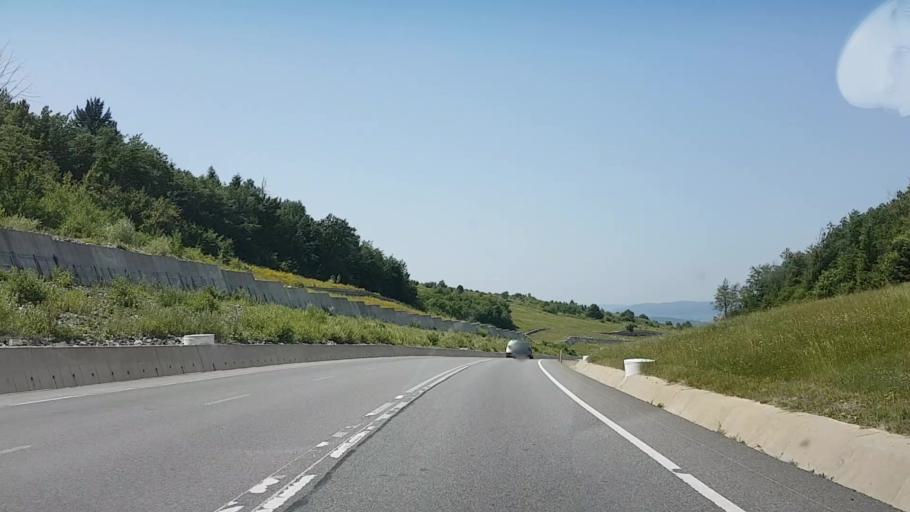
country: RO
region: Cluj
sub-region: Comuna Feleacu
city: Feleacu
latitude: 46.7200
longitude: 23.6513
